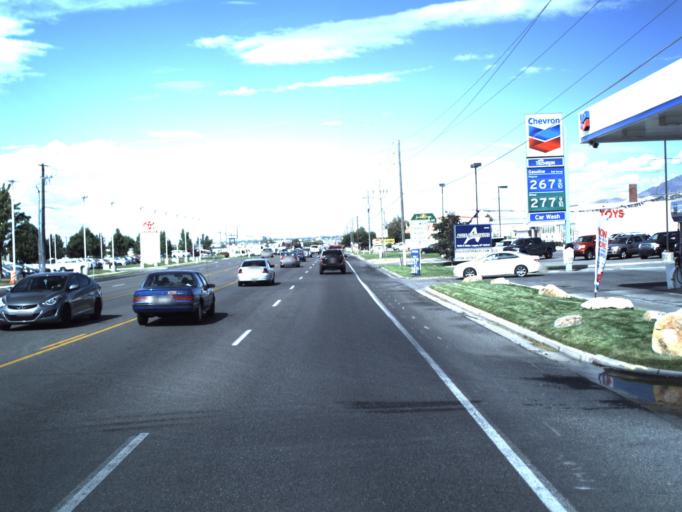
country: US
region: Utah
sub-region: Cache County
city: North Logan
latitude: 41.7661
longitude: -111.8341
